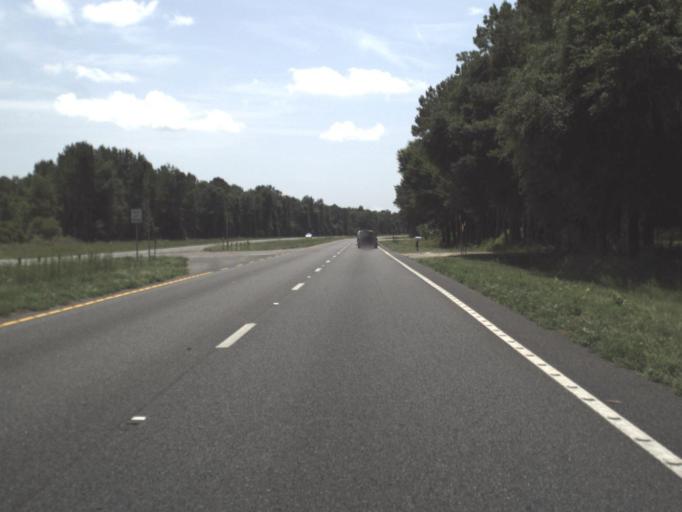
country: US
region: Florida
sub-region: Taylor County
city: Perry
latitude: 29.9952
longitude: -83.5027
